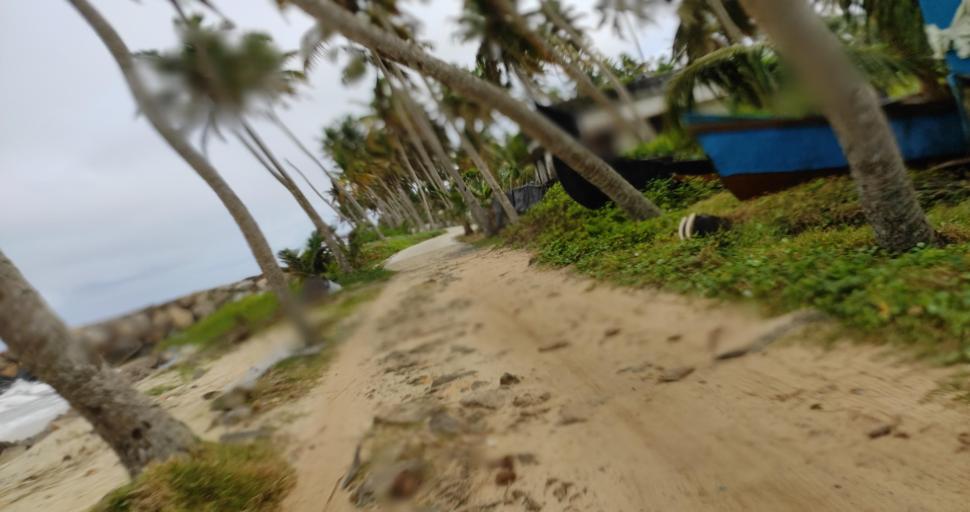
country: IN
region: Kerala
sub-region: Alappuzha
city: Vayalar
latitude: 9.6760
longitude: 76.2913
